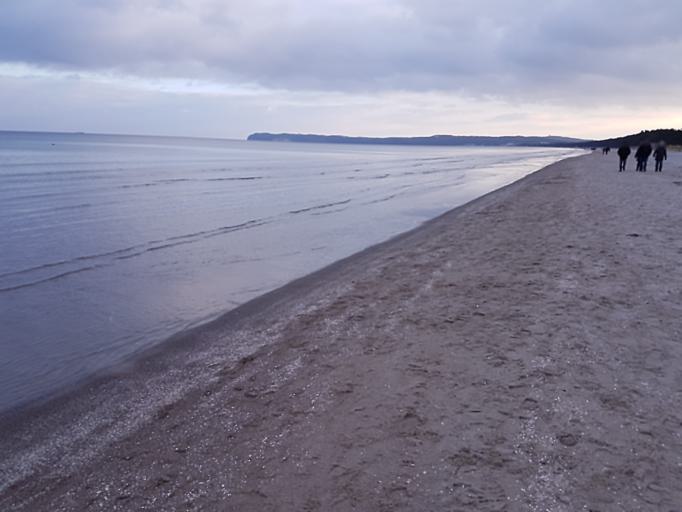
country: DE
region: Mecklenburg-Vorpommern
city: Ostseebad Binz
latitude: 54.4355
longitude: 13.5803
